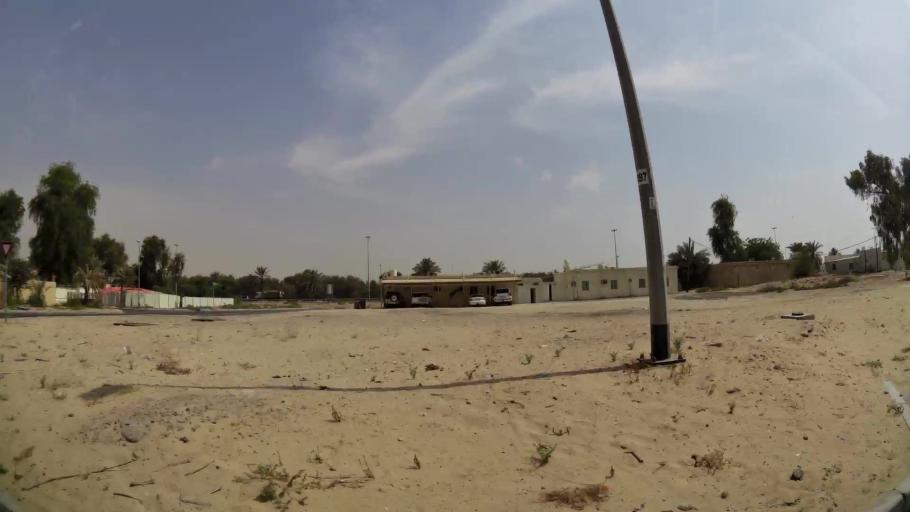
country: AE
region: Ash Shariqah
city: Sharjah
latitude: 25.2330
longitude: 55.4443
